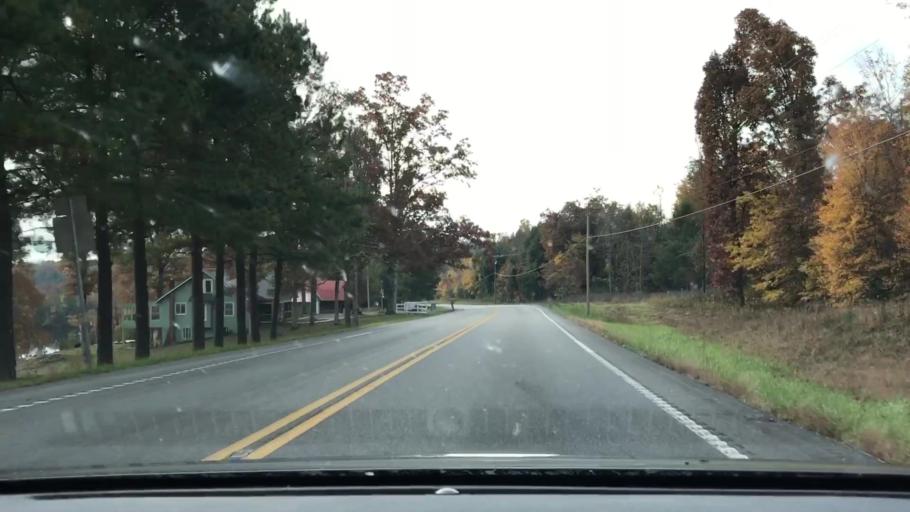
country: US
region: Tennessee
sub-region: Putnam County
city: Monterey
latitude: 36.1260
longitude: -85.2004
